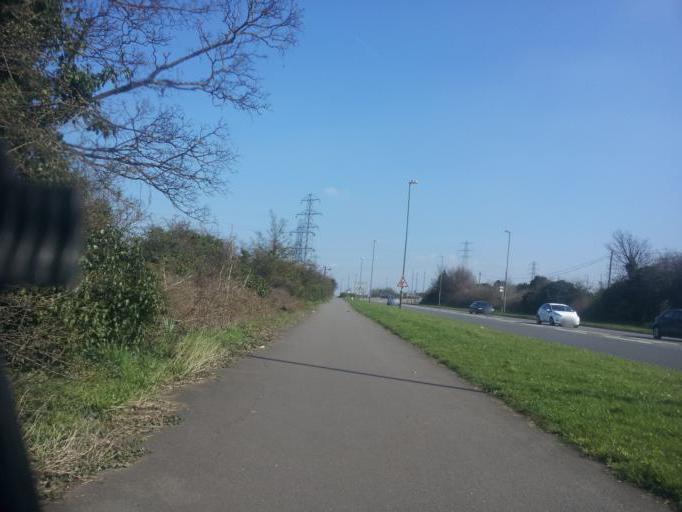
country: GB
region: England
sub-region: Kent
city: Stone
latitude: 51.4378
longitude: 0.2581
